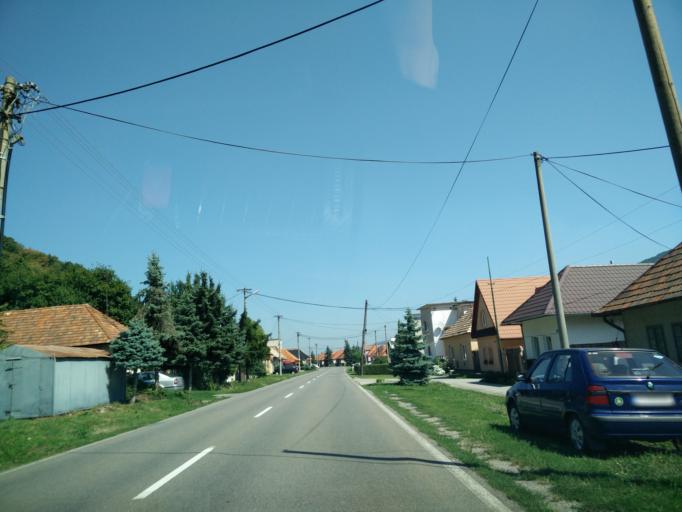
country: SK
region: Nitriansky
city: Tlmace
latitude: 48.3472
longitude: 18.5614
